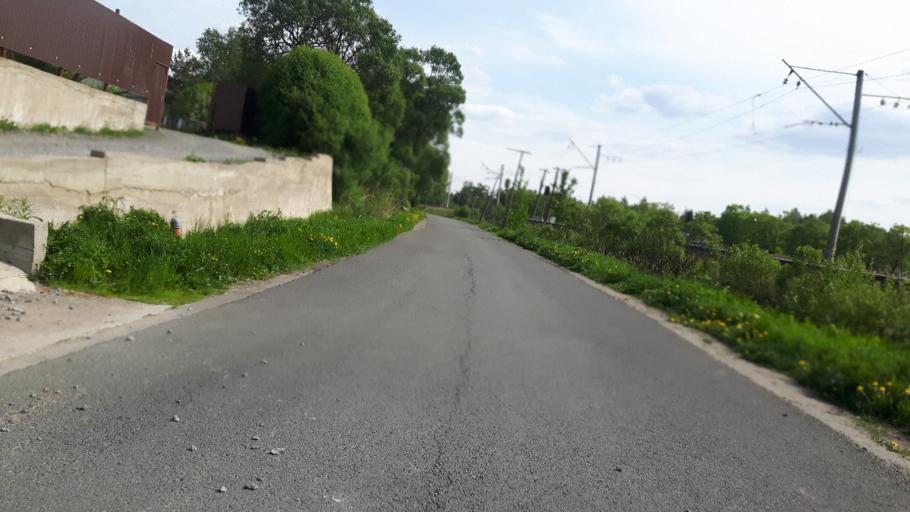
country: RU
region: Leningrad
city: Gorskaya
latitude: 60.0355
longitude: 29.9805
